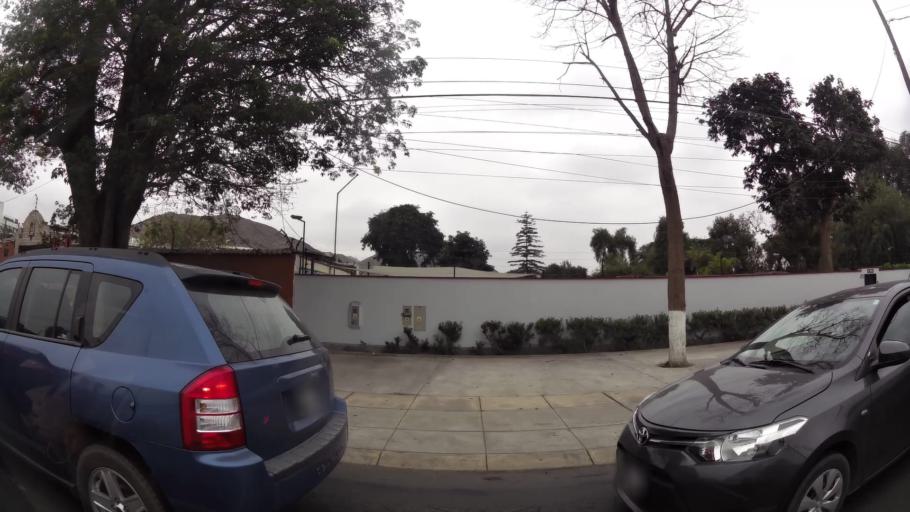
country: PE
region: Lima
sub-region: Lima
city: La Molina
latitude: -12.0758
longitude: -76.9592
